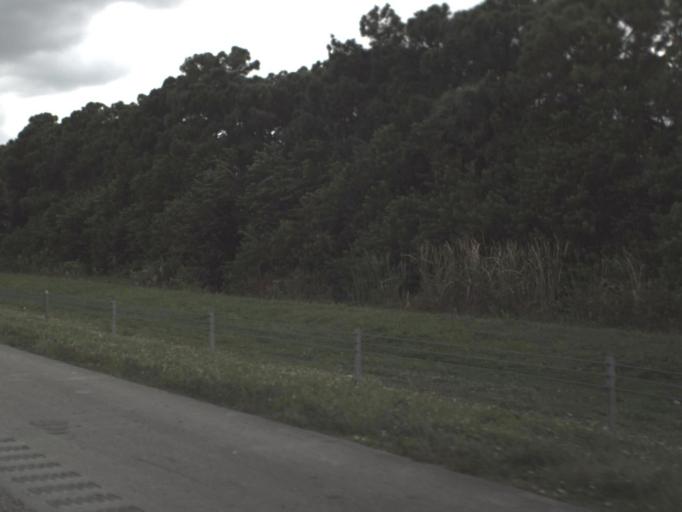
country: US
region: Florida
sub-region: Palm Beach County
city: Palm Beach Gardens
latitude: 26.7800
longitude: -80.1326
